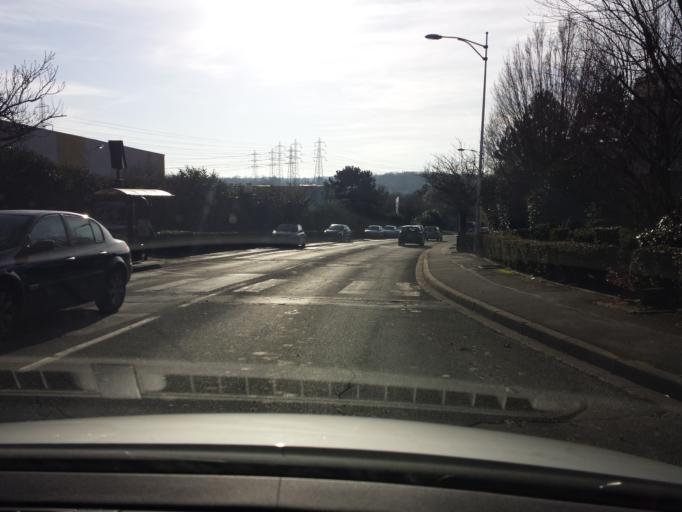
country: FR
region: Ile-de-France
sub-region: Departement de l'Essonne
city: Palaiseau
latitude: 48.7104
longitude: 2.2568
